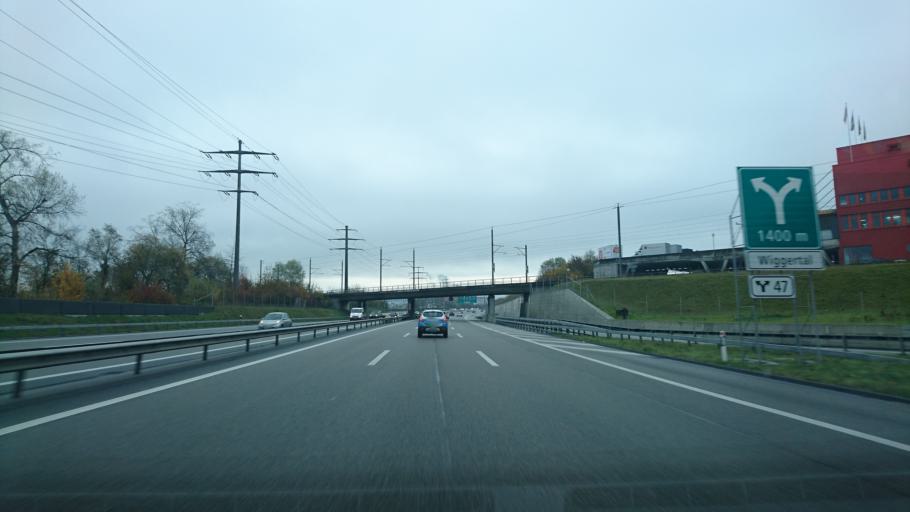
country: CH
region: Aargau
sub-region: Bezirk Zofingen
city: Rothrist
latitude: 47.3119
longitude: 7.8966
